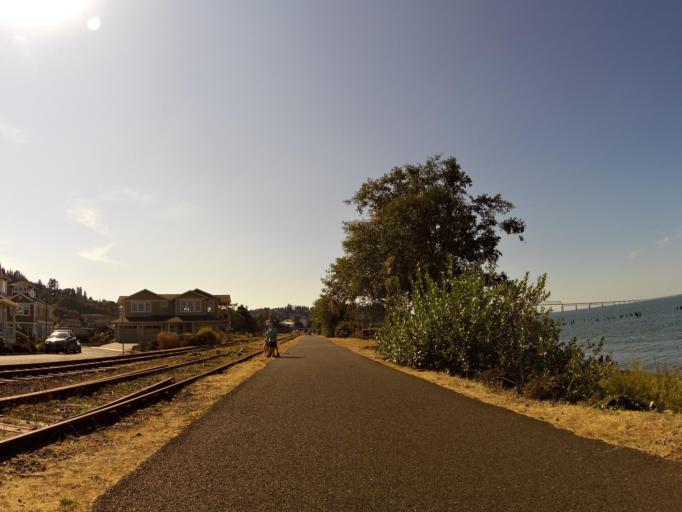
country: US
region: Oregon
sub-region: Clatsop County
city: Astoria
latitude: 46.1916
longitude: -123.8140
